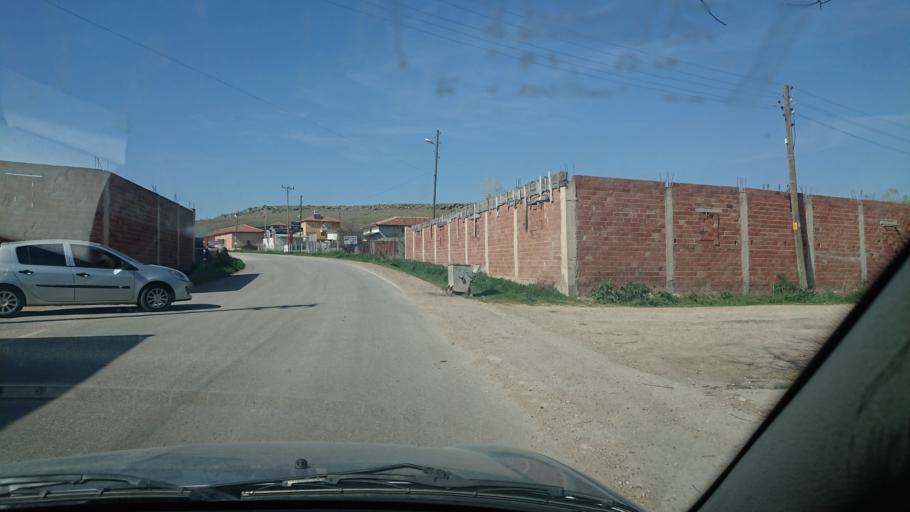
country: TR
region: Eskisehir
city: Eskisehir
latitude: 39.6794
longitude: 30.4861
